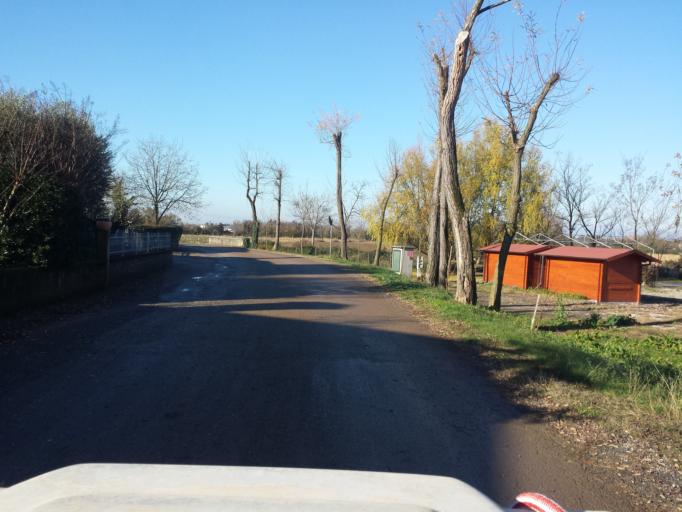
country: IT
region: Friuli Venezia Giulia
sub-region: Provincia di Udine
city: Manzano
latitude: 45.9751
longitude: 13.3795
